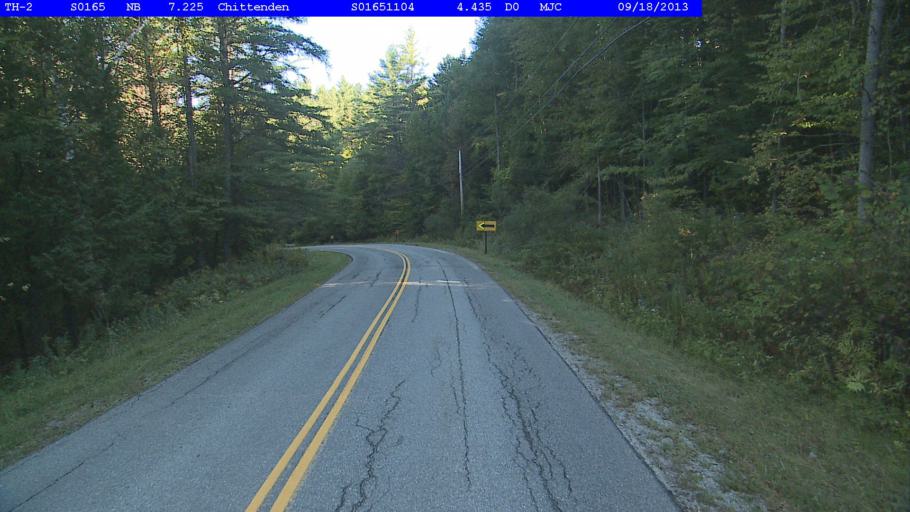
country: US
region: Vermont
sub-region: Rutland County
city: Rutland
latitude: 43.7378
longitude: -72.9705
